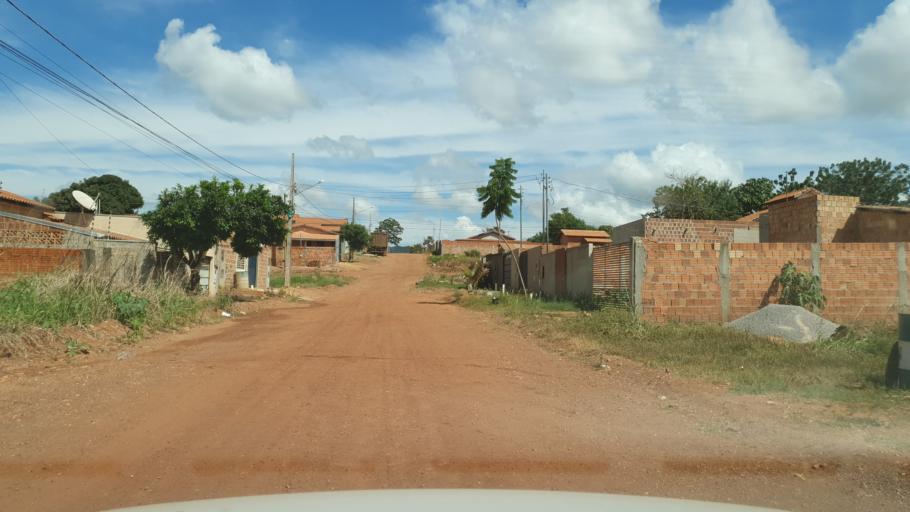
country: BR
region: Mato Grosso
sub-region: Pontes E Lacerda
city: Pontes e Lacerda
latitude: -15.2503
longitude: -59.3135
